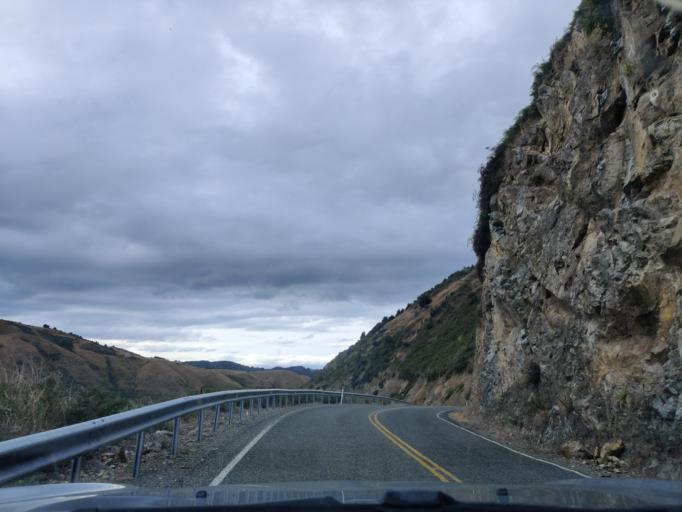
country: NZ
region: Tasman
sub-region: Tasman District
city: Wakefield
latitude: -41.7045
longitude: 172.6689
